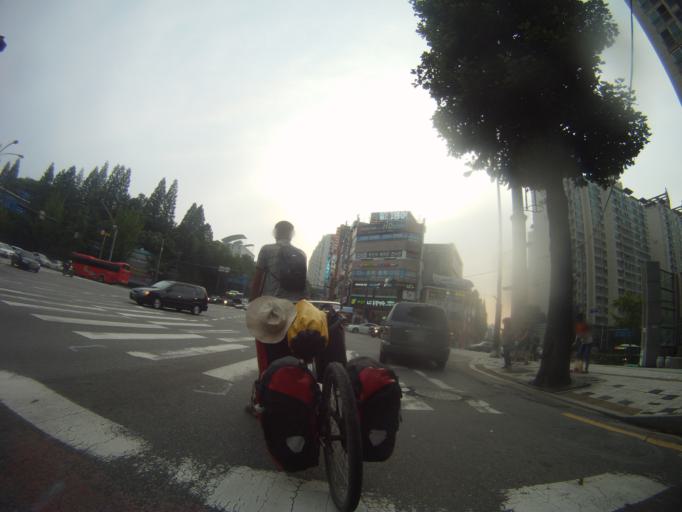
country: KR
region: Incheon
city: Incheon
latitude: 37.4568
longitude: 126.7042
